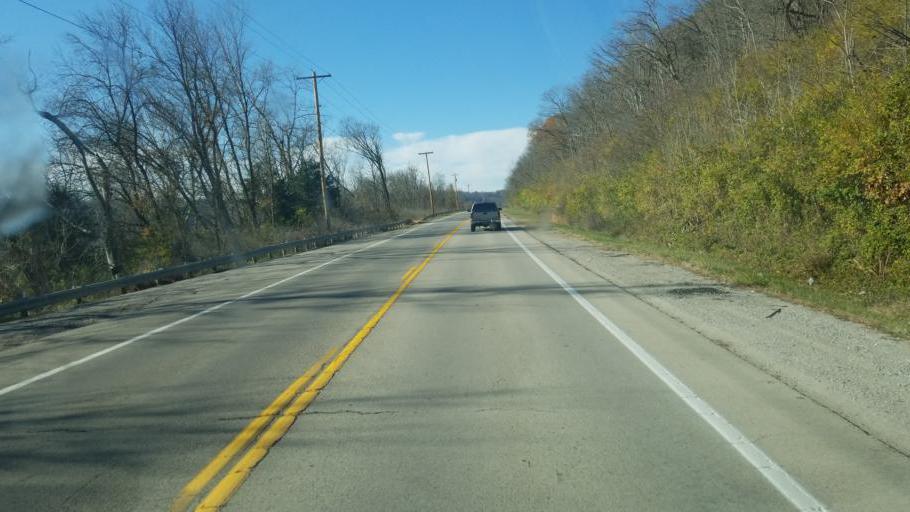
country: US
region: Kentucky
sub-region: Mason County
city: Maysville
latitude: 38.6501
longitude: -83.7442
